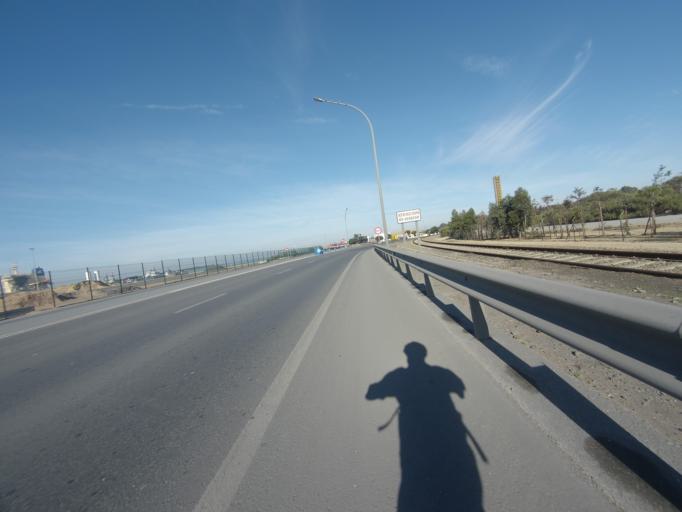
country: ES
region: Andalusia
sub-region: Provincia de Huelva
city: Punta Umbria
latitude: 37.1978
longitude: -6.9341
